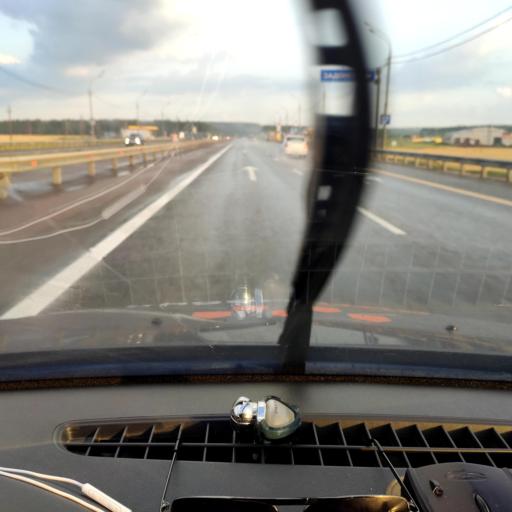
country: RU
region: Lipetsk
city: Zadonsk
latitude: 52.3746
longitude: 38.8982
